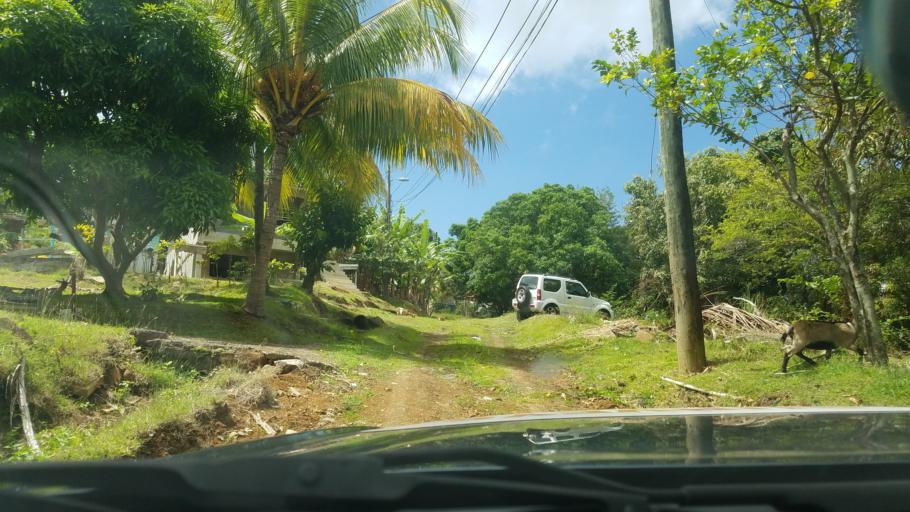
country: LC
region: Gros-Islet
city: Gros Islet
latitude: 14.0601
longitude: -60.9491
